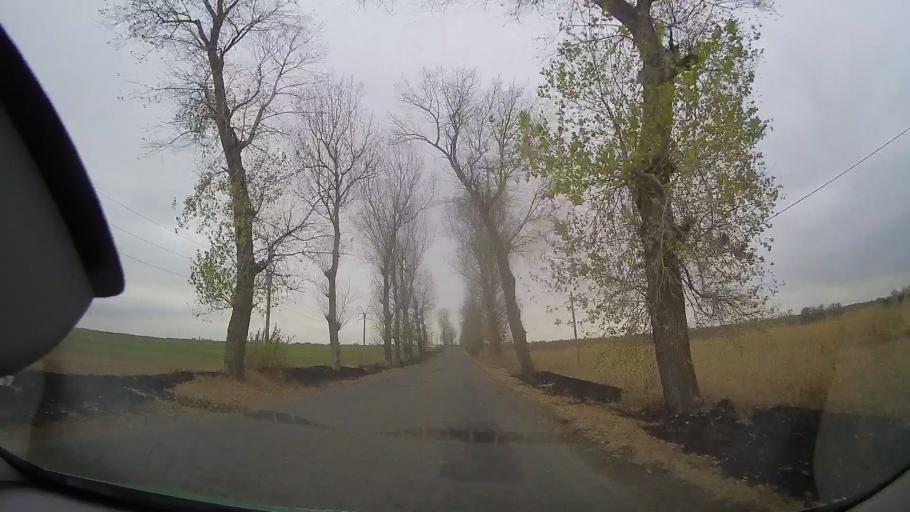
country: RO
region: Buzau
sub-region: Comuna Rusetu
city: Rusetu
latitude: 44.9489
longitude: 27.2290
